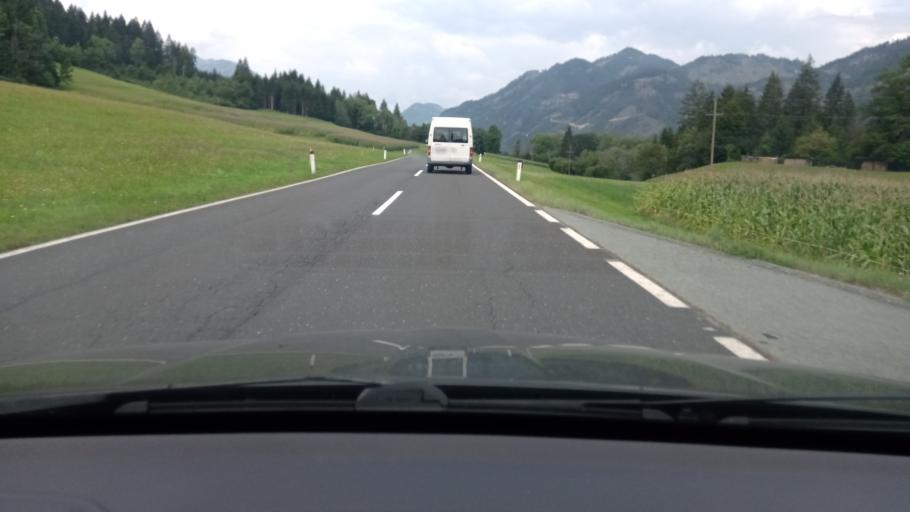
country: AT
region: Carinthia
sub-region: Politischer Bezirk Hermagor
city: Hermagor
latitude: 46.6546
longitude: 13.3226
